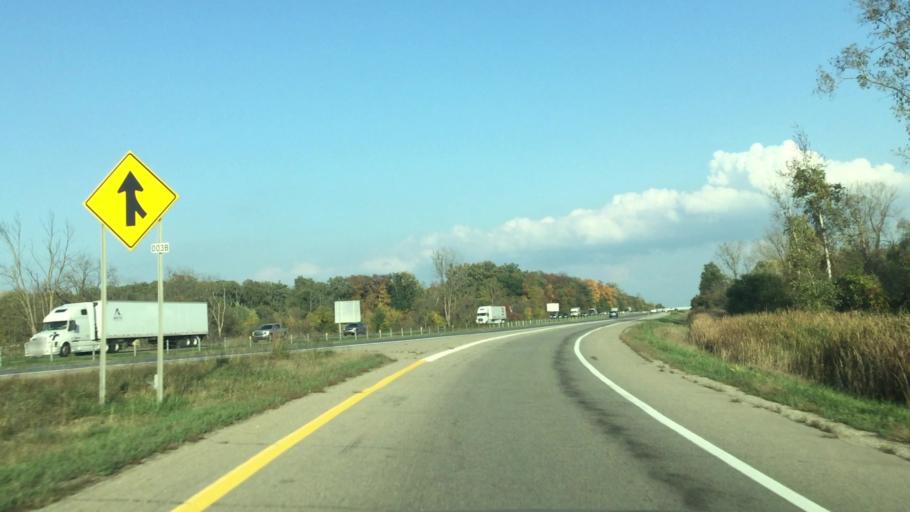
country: US
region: Michigan
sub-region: Washtenaw County
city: Chelsea
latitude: 42.2946
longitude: -84.0223
